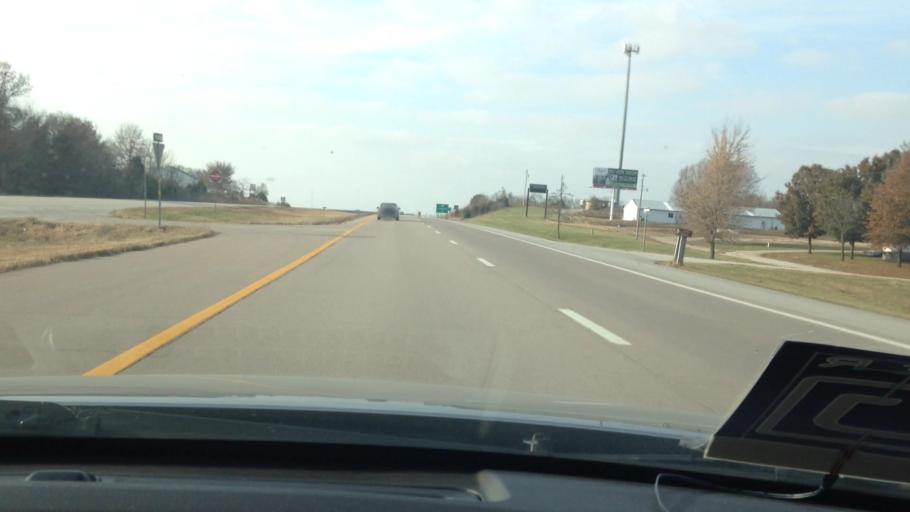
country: US
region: Missouri
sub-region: Cass County
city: Garden City
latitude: 38.4971
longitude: -94.0638
